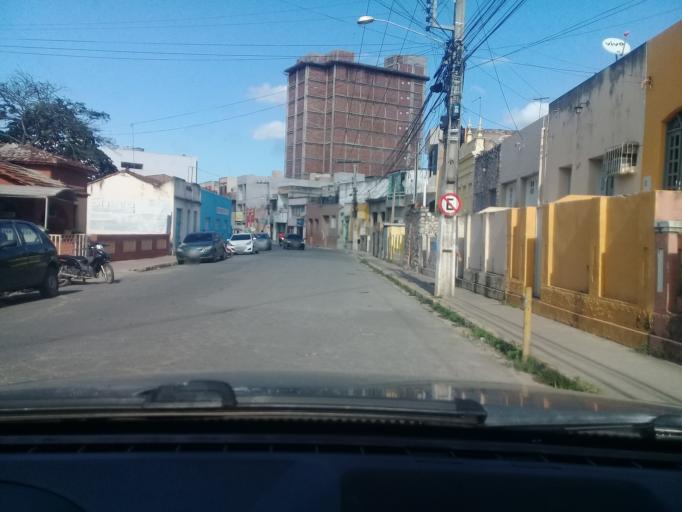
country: BR
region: Pernambuco
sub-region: Vitoria De Santo Antao
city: Vitoria de Santo Antao
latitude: -8.1200
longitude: -35.3005
